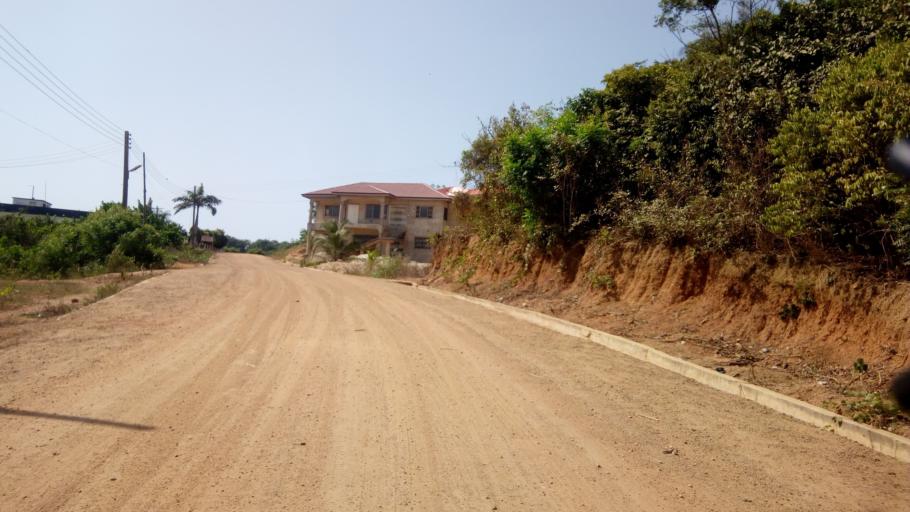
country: GH
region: Central
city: Cape Coast
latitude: 5.1115
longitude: -1.2680
